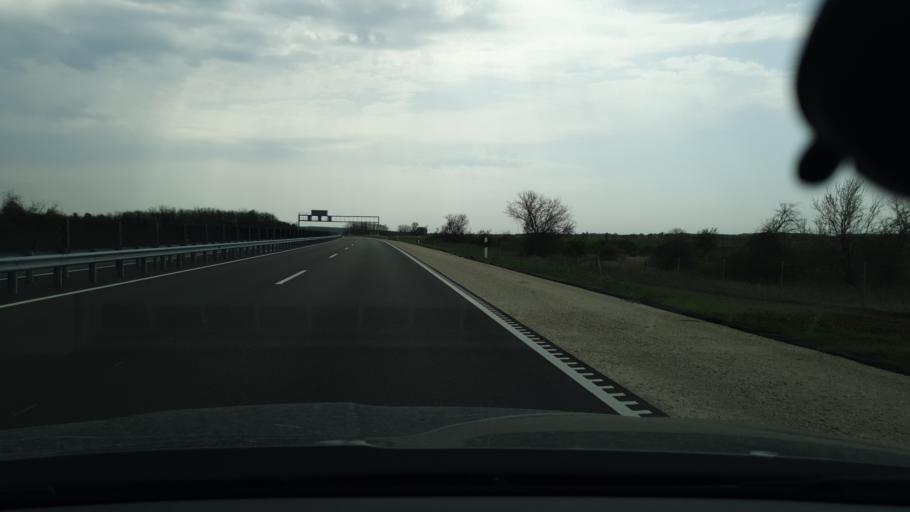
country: HU
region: Pest
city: Gomba
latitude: 47.3372
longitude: 19.5070
